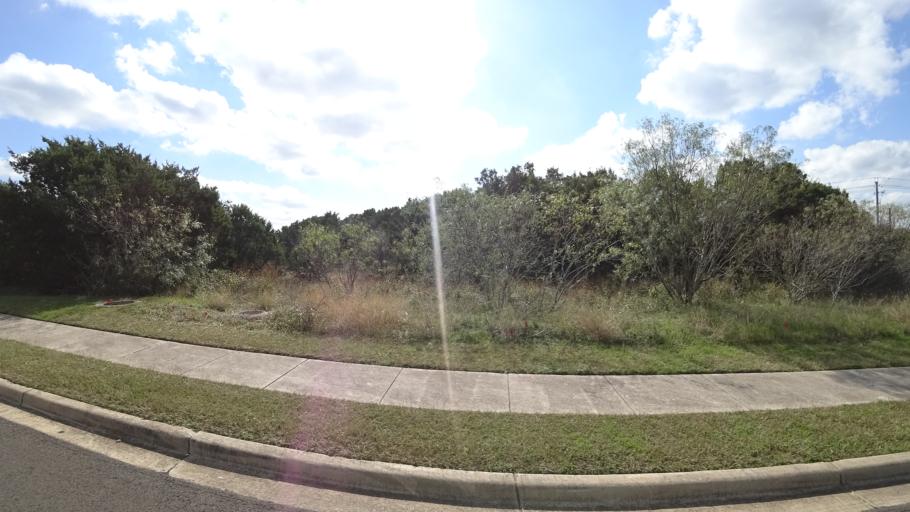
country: US
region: Texas
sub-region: Travis County
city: Barton Creek
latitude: 30.2548
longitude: -97.8885
